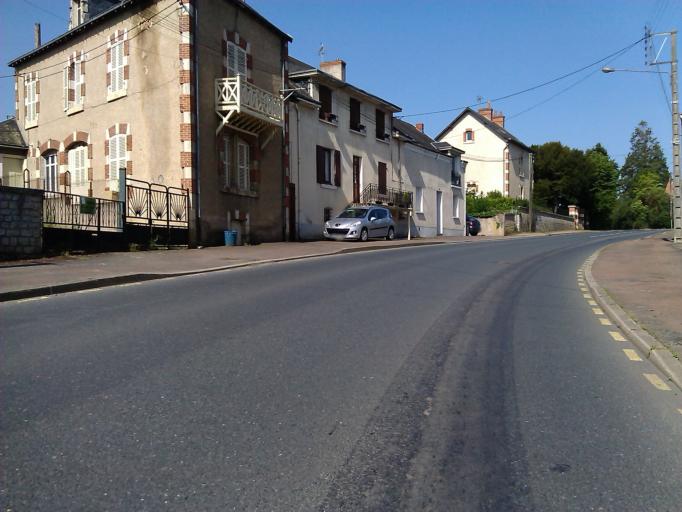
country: FR
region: Centre
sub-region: Departement de l'Indre
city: Neuvy-Saint-Sepulchre
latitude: 46.5972
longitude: 1.8050
